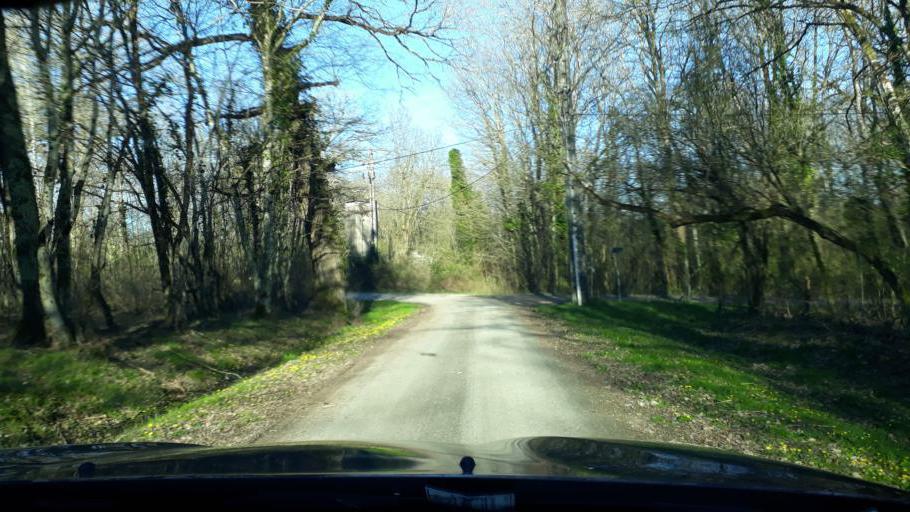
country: FR
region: Centre
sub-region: Departement du Loiret
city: Jouy-le-Potier
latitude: 47.7081
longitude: 1.8336
